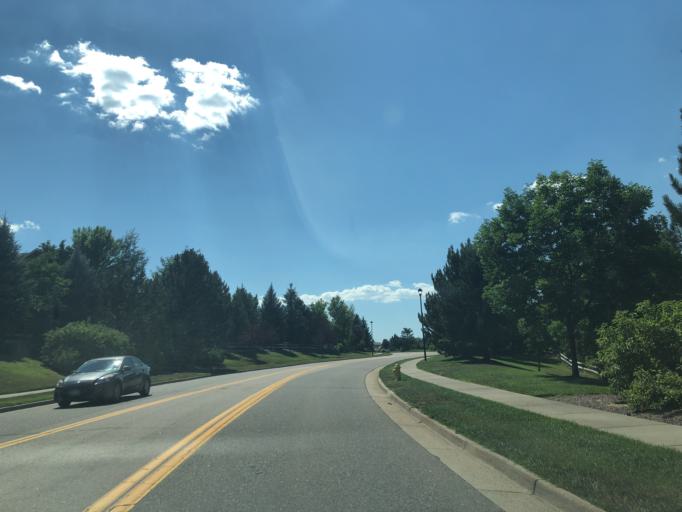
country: US
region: Colorado
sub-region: Arapahoe County
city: Dove Valley
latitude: 39.6031
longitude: -104.7776
